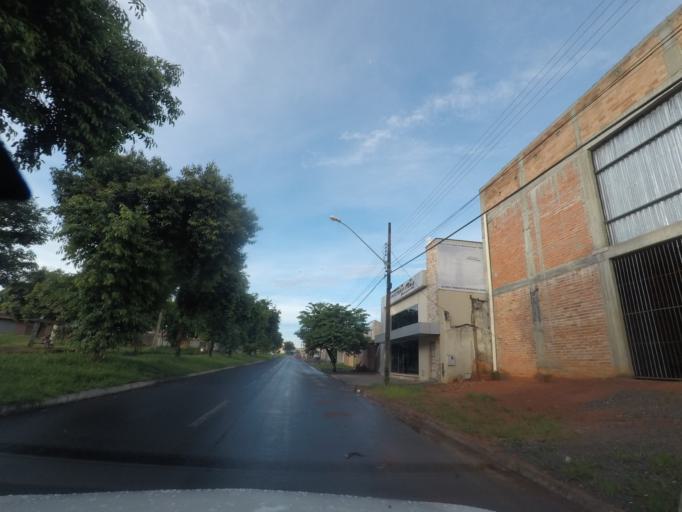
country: BR
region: Goias
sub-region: Goiania
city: Goiania
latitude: -16.7368
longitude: -49.3684
